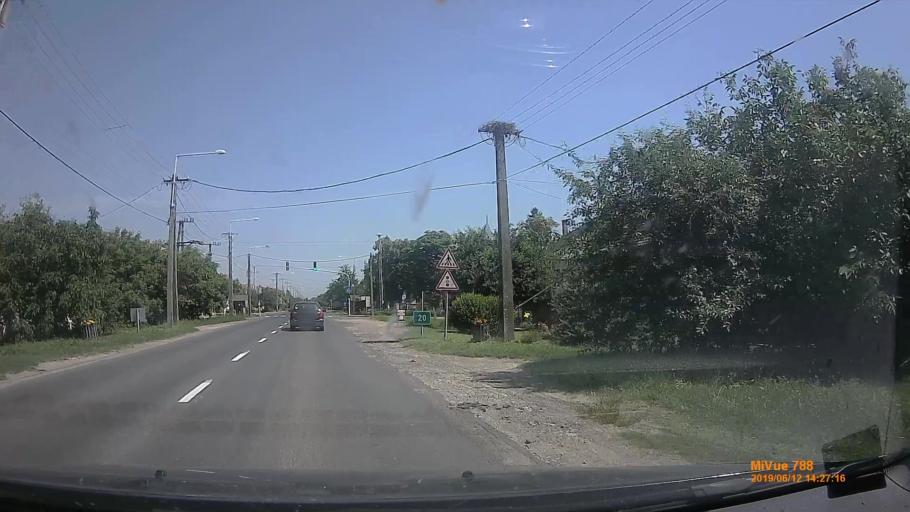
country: HU
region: Csongrad
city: Maroslele
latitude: 46.2177
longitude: 20.3525
